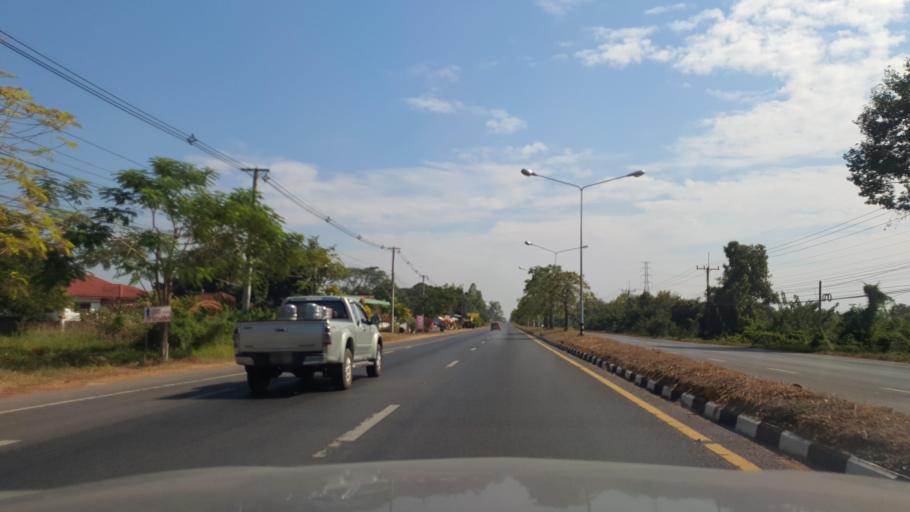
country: TH
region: Maha Sarakham
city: Kantharawichai
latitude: 16.3875
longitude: 103.2517
